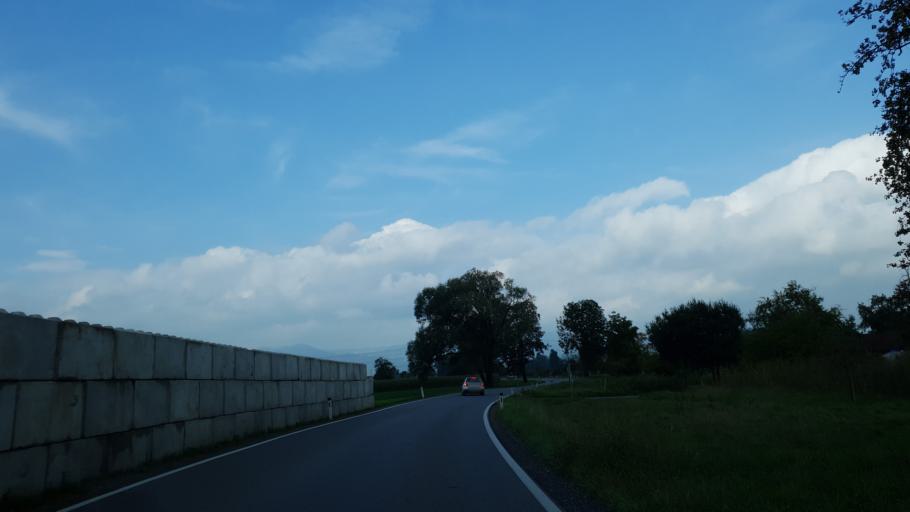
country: AT
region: Vorarlberg
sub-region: Politischer Bezirk Dornbirn
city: Dornbirn
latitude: 47.3992
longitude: 9.7151
